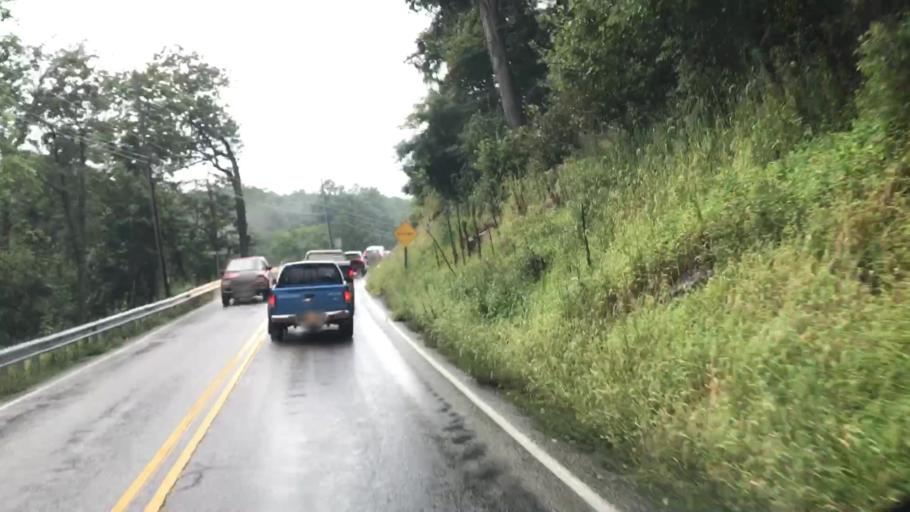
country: US
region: Pennsylvania
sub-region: Cumberland County
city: Schlusser
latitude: 40.2937
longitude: -77.1306
